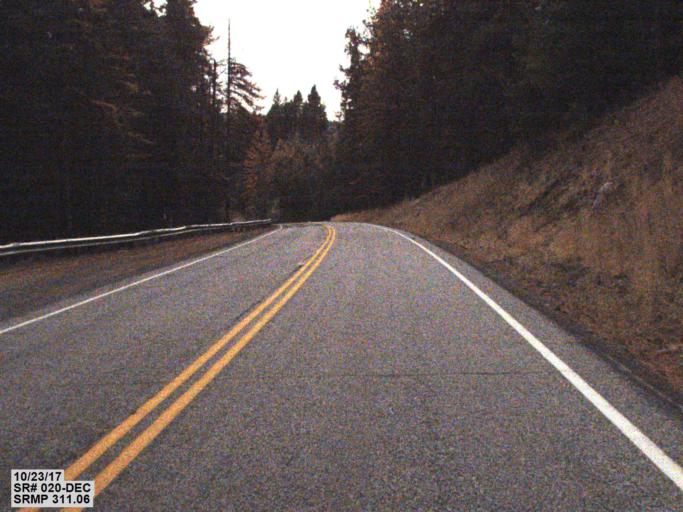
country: US
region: Washington
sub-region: Ferry County
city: Republic
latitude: 48.6016
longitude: -118.6155
